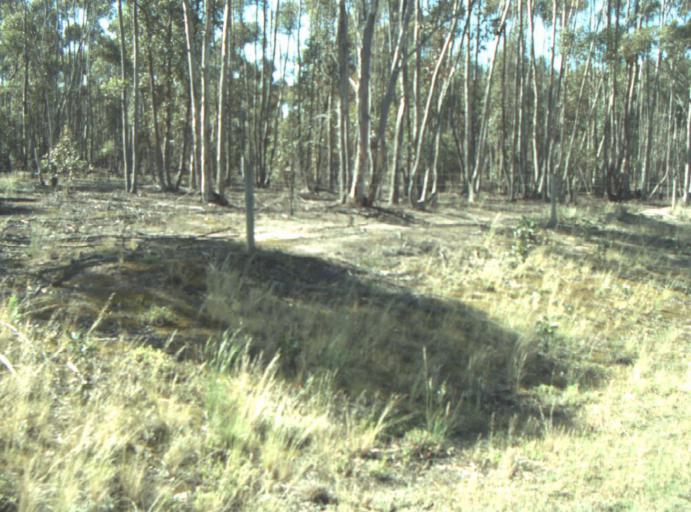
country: AU
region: Victoria
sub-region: Greater Geelong
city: Lara
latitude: -37.9404
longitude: 144.3927
